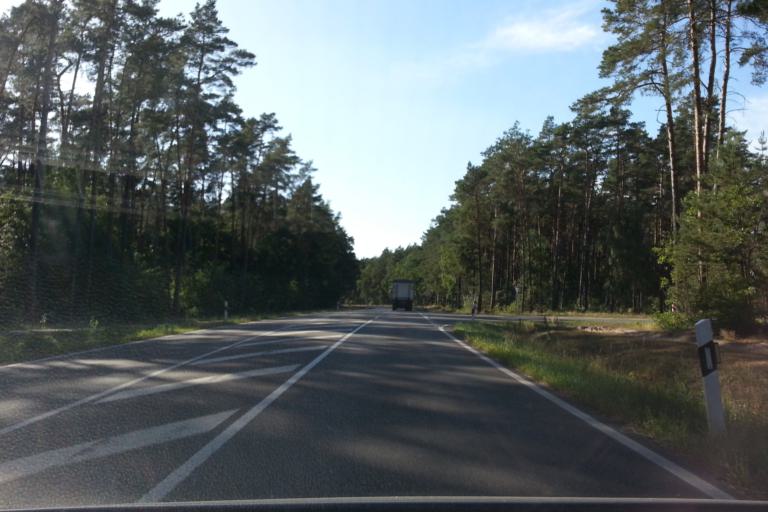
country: DE
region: Mecklenburg-Vorpommern
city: Torgelow
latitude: 53.6328
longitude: 13.9885
